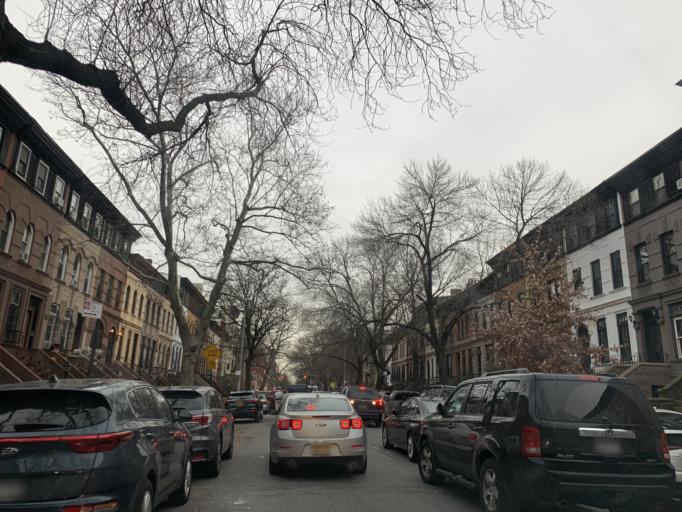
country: US
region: New York
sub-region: Kings County
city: Brooklyn
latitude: 40.6760
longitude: -73.9652
